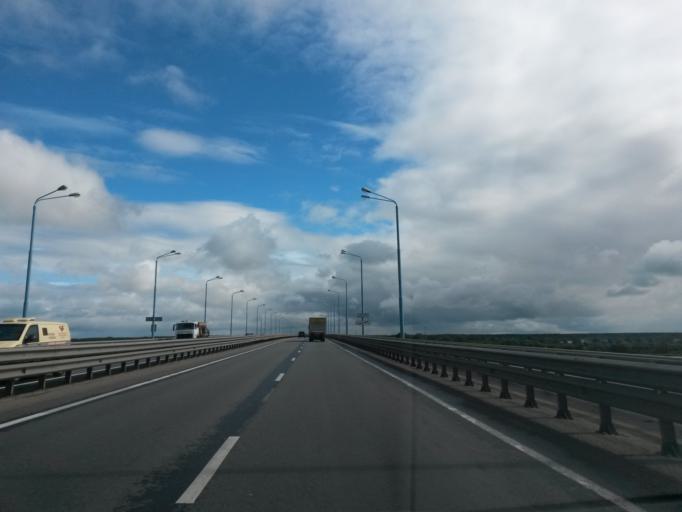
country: RU
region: Jaroslavl
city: Yaroslavl
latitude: 57.6718
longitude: 39.8488
